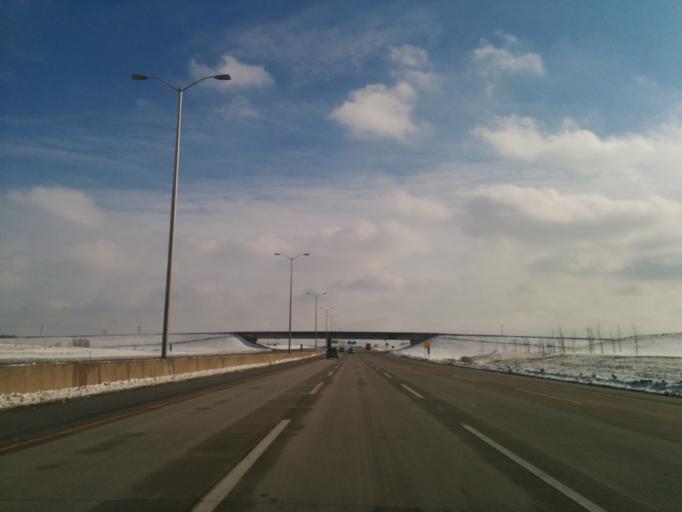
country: US
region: Illinois
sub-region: Will County
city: Lockport
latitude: 41.5717
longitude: -87.9961
